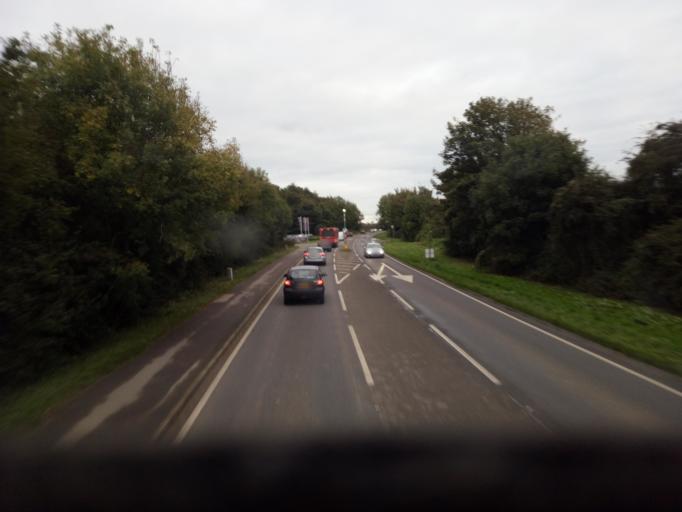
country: GB
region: England
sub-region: West Sussex
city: Boxgrove
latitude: 50.8203
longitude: -0.7171
